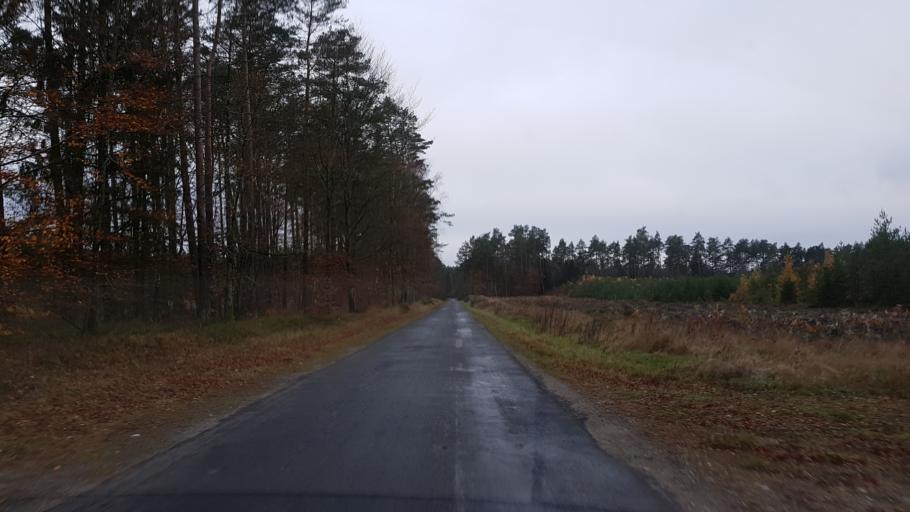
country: PL
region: West Pomeranian Voivodeship
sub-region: Powiat koszalinski
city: Bobolice
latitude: 54.0704
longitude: 16.5698
